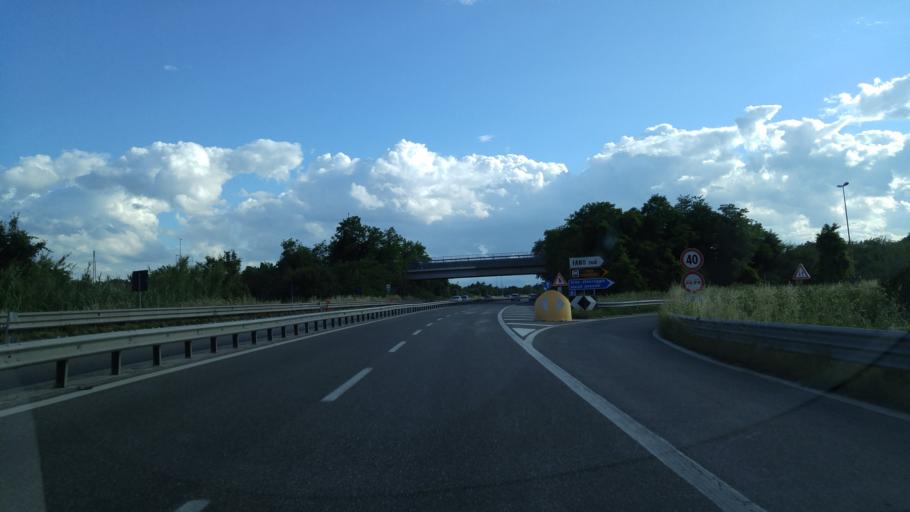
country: IT
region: The Marches
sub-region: Provincia di Pesaro e Urbino
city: Bellocchi
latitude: 43.8069
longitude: 13.0174
